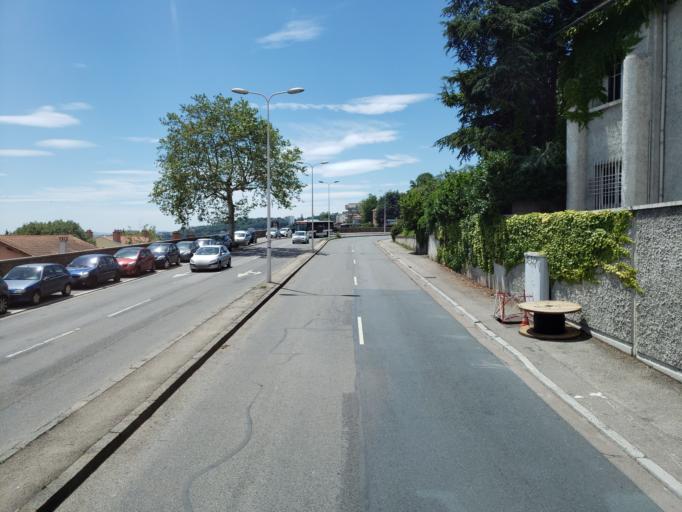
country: FR
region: Rhone-Alpes
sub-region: Departement du Rhone
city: Sainte-Foy-les-Lyon
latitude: 45.7515
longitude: 4.8162
